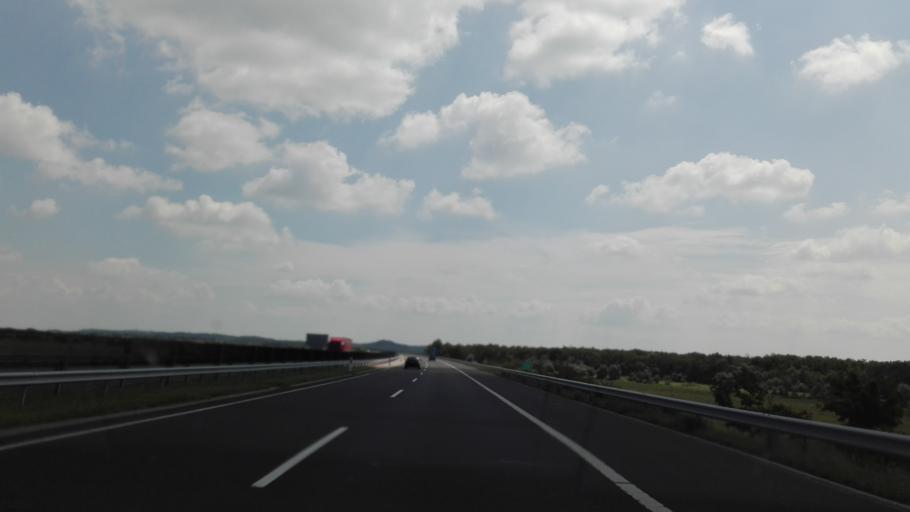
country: HU
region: Fejer
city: Adony
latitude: 47.1023
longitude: 18.8447
